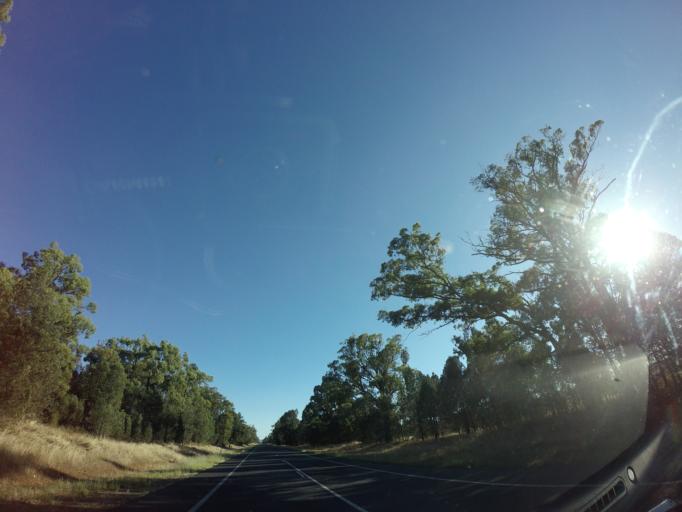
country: AU
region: New South Wales
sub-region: Gilgandra
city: Gilgandra
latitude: -31.5536
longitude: 148.8145
